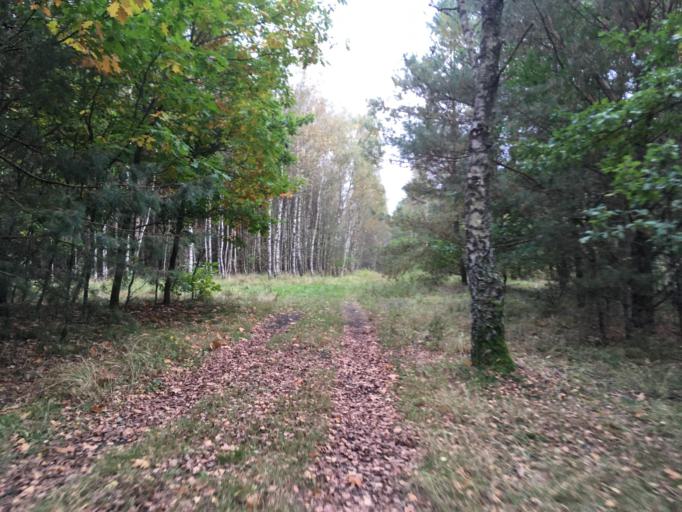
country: DE
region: Brandenburg
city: Birkenwerder
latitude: 52.7031
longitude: 13.3488
